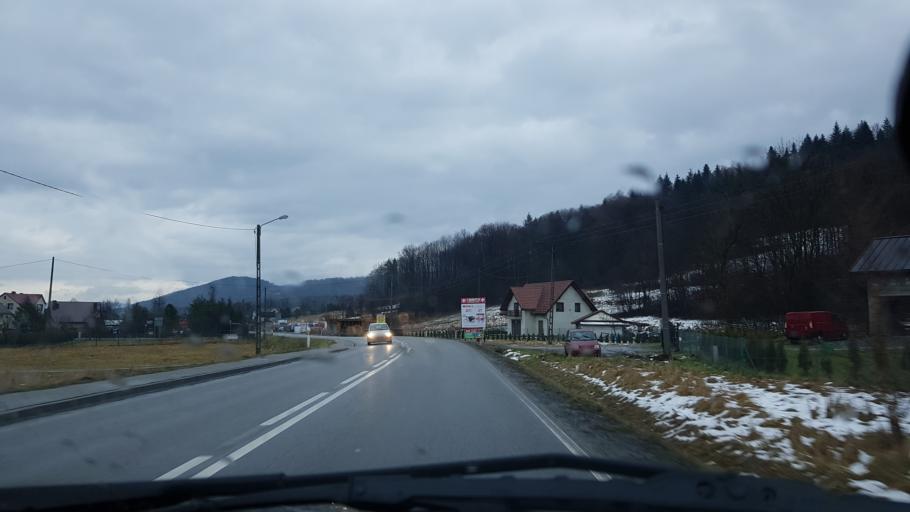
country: PL
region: Lesser Poland Voivodeship
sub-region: Powiat suski
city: Kukow
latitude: 49.7285
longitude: 19.4952
